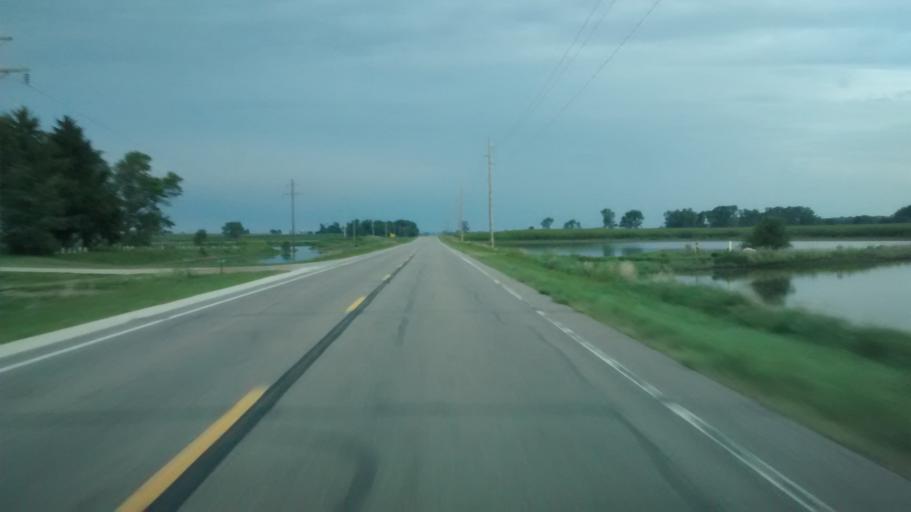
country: US
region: Iowa
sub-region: Woodbury County
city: Moville
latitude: 42.5407
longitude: -96.0287
